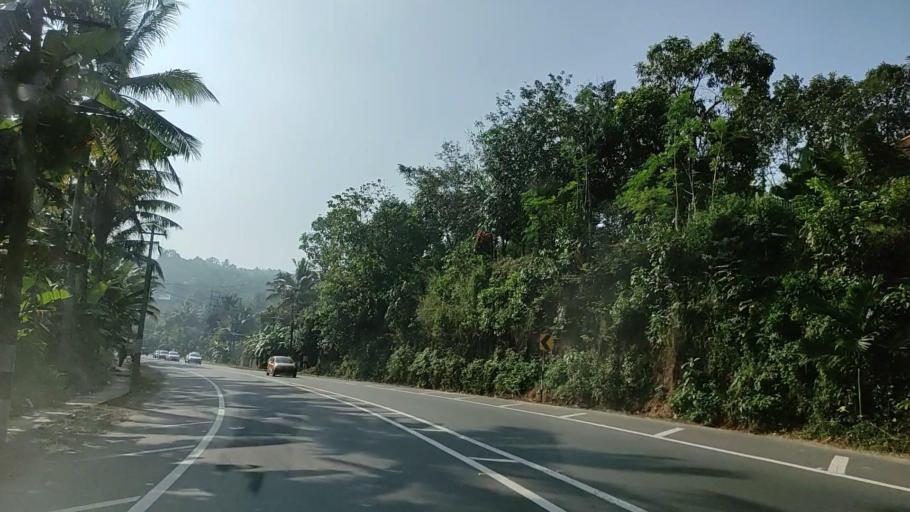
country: IN
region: Kerala
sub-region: Kollam
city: Punalur
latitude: 8.9703
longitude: 76.8287
